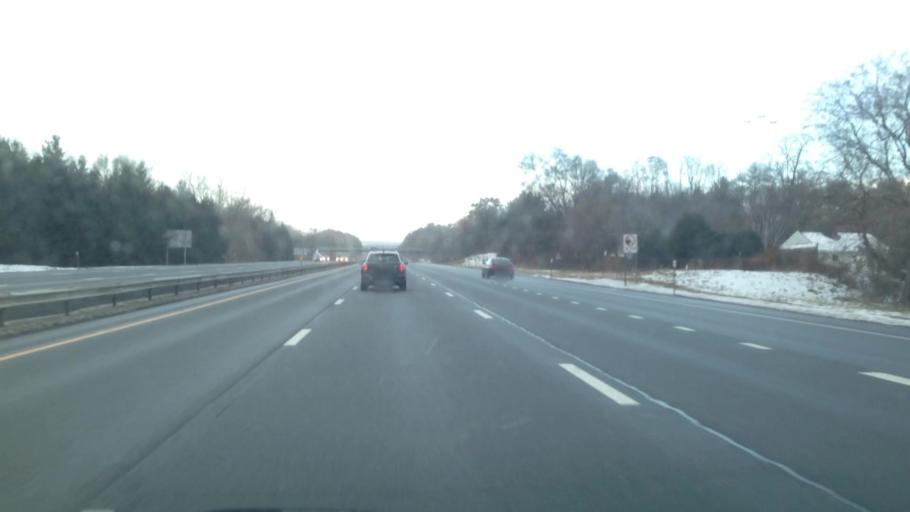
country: US
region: New York
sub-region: Schenectady County
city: Rotterdam
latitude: 42.7563
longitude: -73.9380
